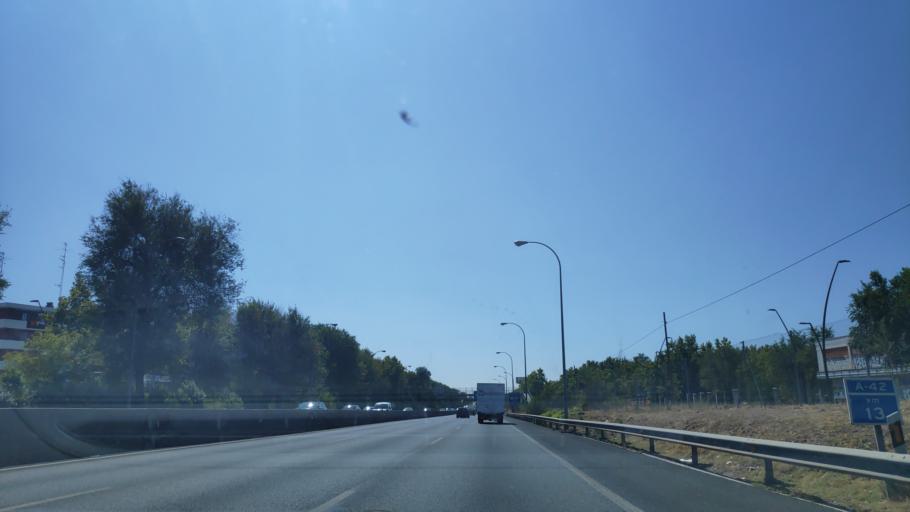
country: ES
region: Madrid
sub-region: Provincia de Madrid
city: Getafe
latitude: 40.3079
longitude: -3.7403
